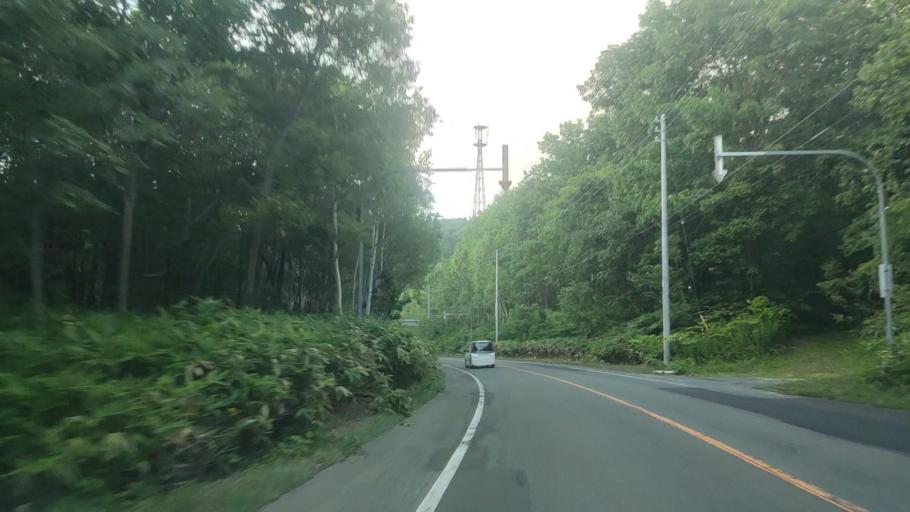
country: JP
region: Hokkaido
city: Ashibetsu
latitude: 43.3785
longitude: 142.1770
